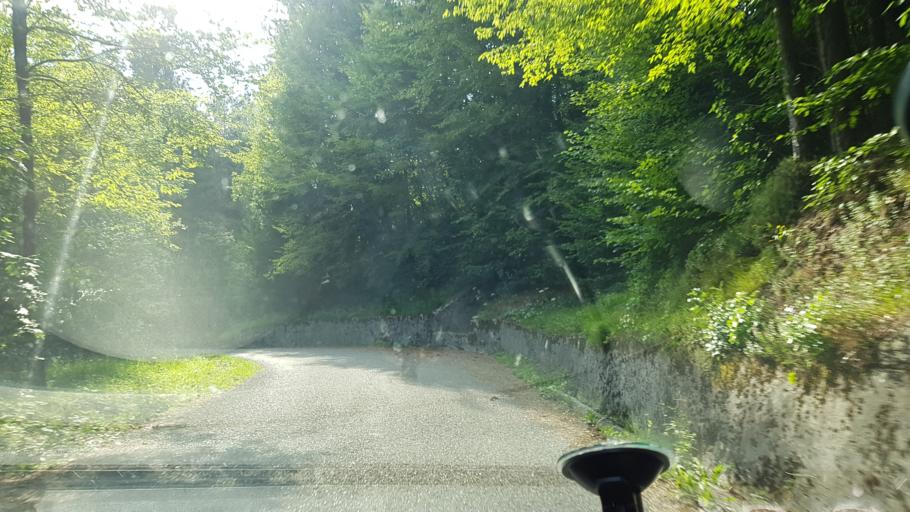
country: IT
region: Friuli Venezia Giulia
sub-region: Provincia di Udine
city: Prato
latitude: 46.3579
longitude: 13.3672
